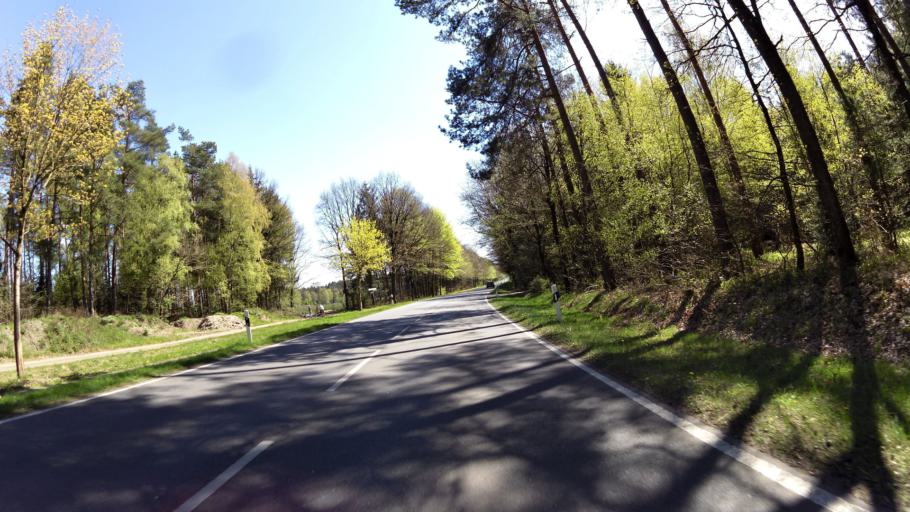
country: DE
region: Lower Saxony
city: Soltau
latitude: 53.0075
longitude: 9.8006
